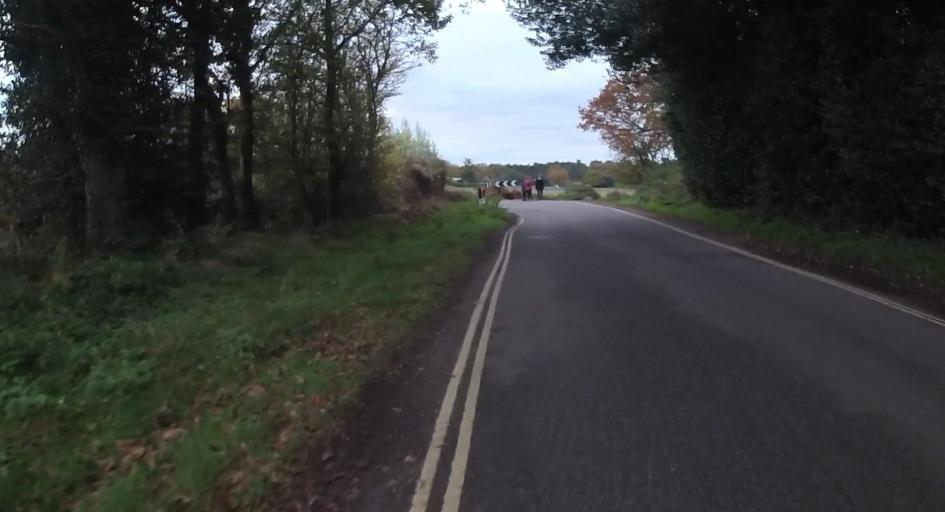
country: GB
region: England
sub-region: Surrey
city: Churt
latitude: 51.1505
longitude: -0.8000
